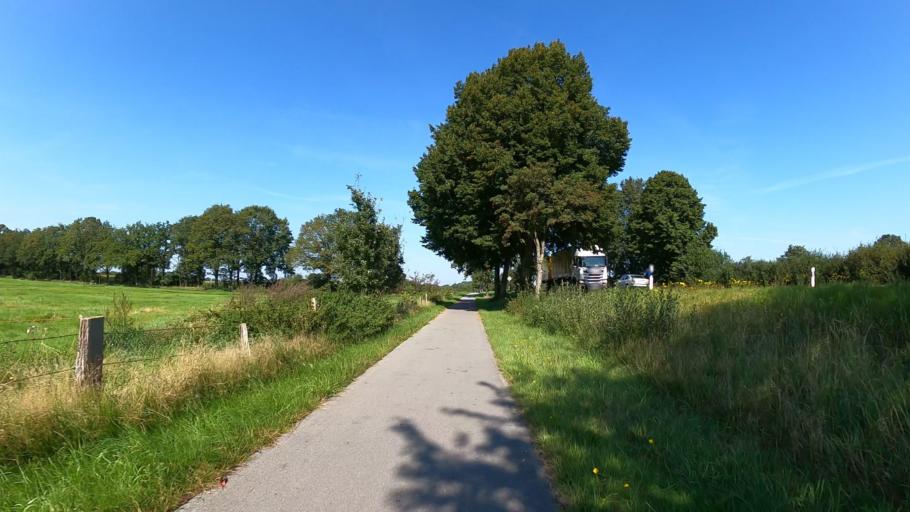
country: DE
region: Schleswig-Holstein
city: Lentfohrden
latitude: 53.8881
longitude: 9.8857
